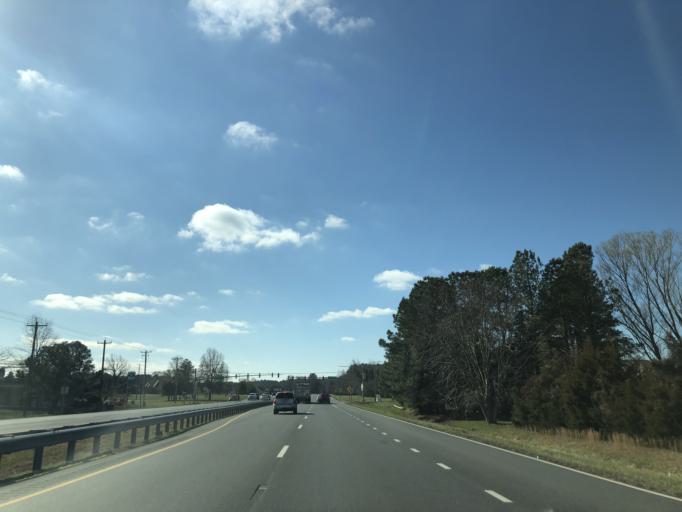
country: US
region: Maryland
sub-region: Worcester County
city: Berlin
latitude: 38.3255
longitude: -75.2113
